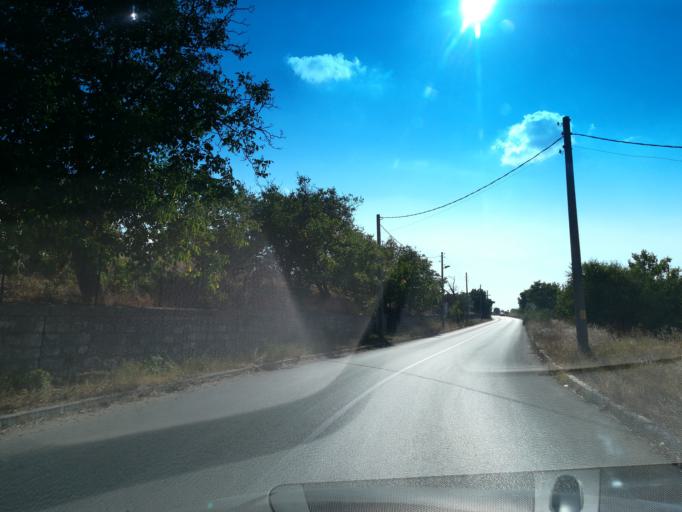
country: BG
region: Khaskovo
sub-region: Obshtina Mineralni Bani
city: Mineralni Bani
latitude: 42.0035
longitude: 25.3805
